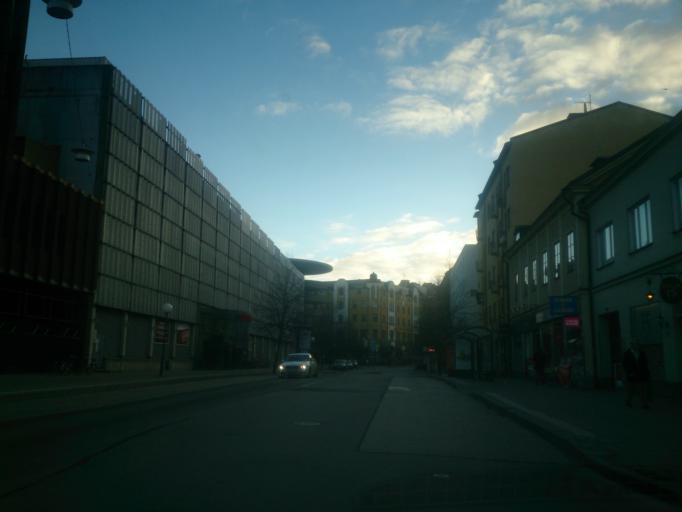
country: SE
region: OEstergoetland
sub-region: Norrkopings Kommun
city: Norrkoping
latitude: 58.5876
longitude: 16.1873
